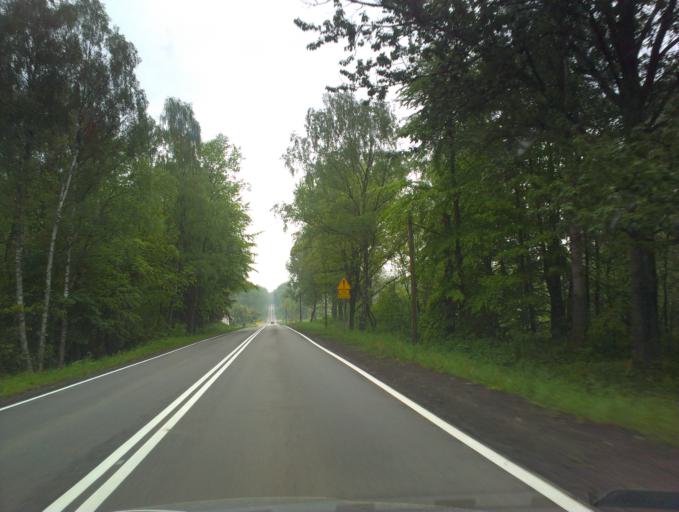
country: PL
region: West Pomeranian Voivodeship
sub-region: Powiat koszalinski
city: Bobolice
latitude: 53.9102
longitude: 16.6092
